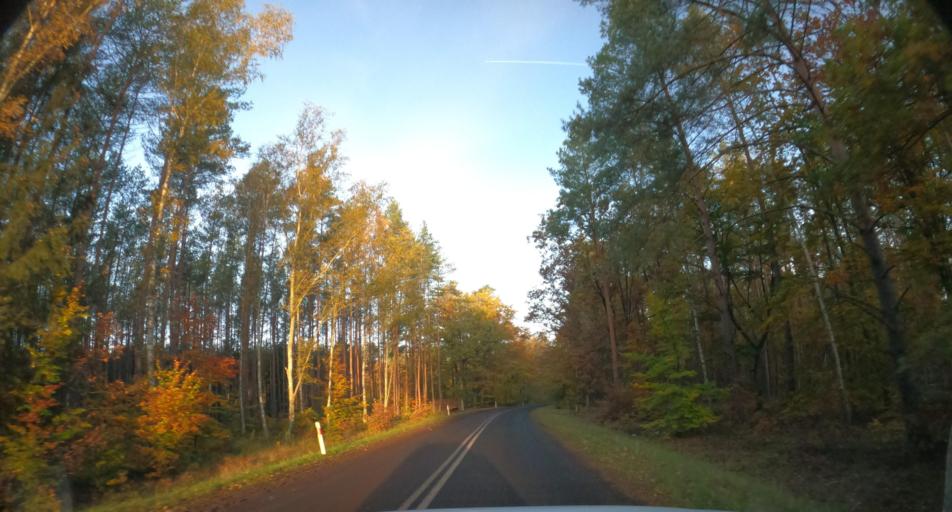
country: PL
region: West Pomeranian Voivodeship
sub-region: Powiat policki
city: Nowe Warpno
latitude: 53.6047
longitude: 14.3208
